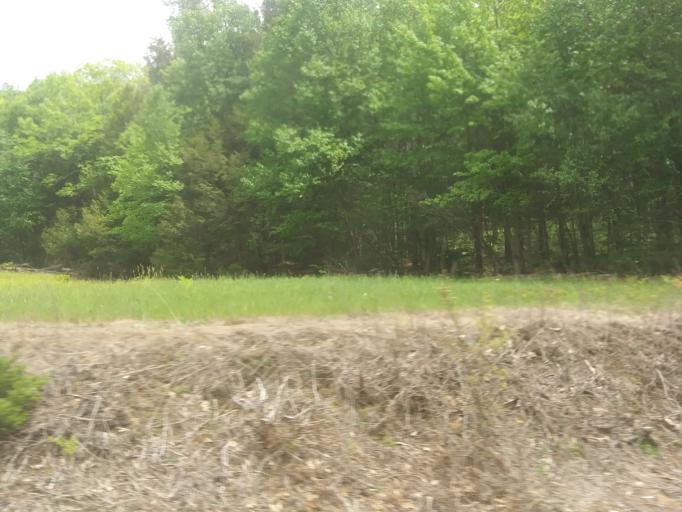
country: US
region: Massachusetts
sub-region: Franklin County
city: Shelburne Falls
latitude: 42.5962
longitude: -72.7609
